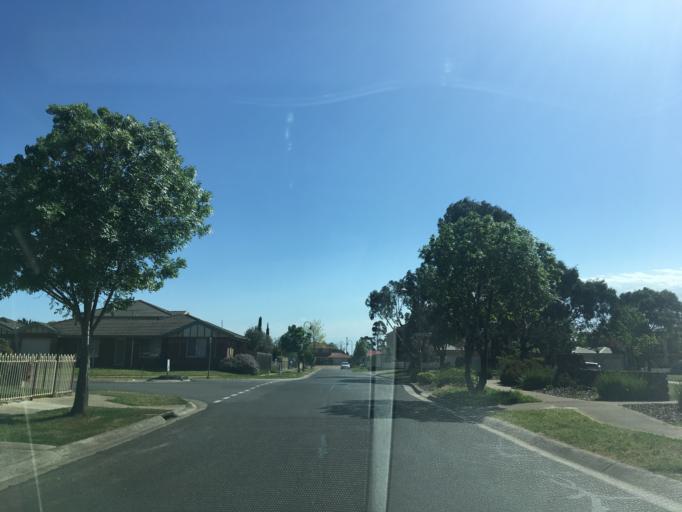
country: AU
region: Victoria
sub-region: Wyndham
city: Hoppers Crossing
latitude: -37.8777
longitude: 144.7038
